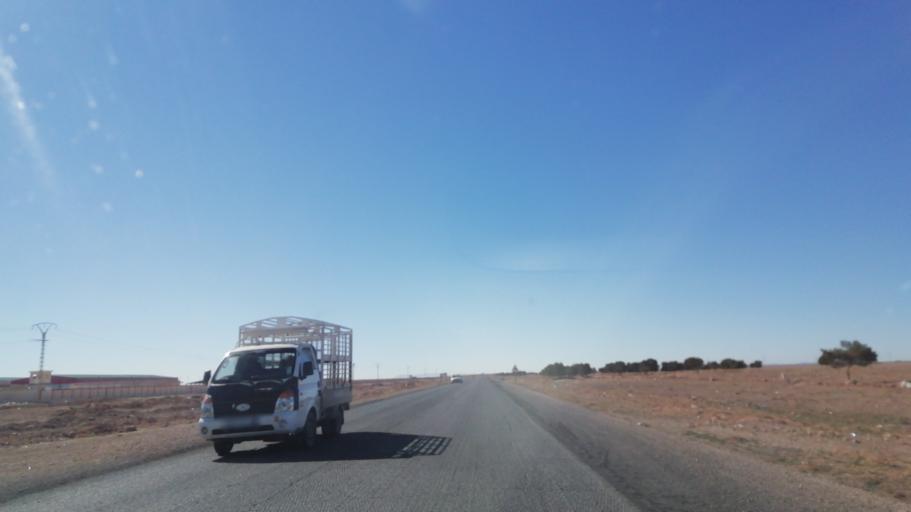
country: DZ
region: Saida
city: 'Ain el Hadjar
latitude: 34.0241
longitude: 0.0676
